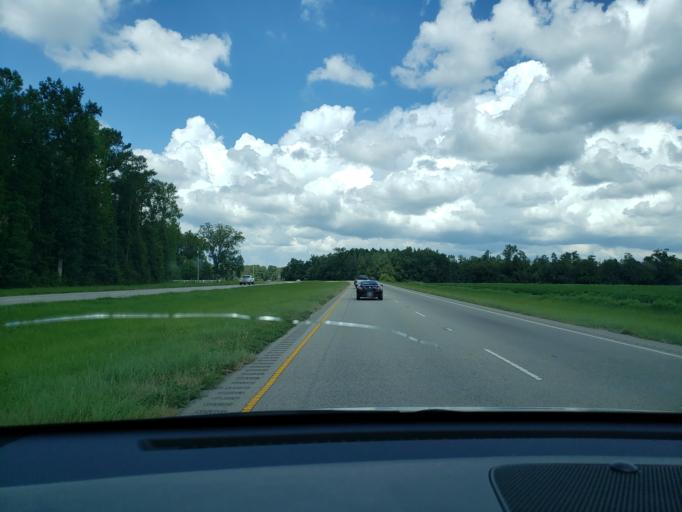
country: US
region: North Carolina
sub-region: Bladen County
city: Elizabethtown
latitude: 34.7004
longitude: -78.7396
